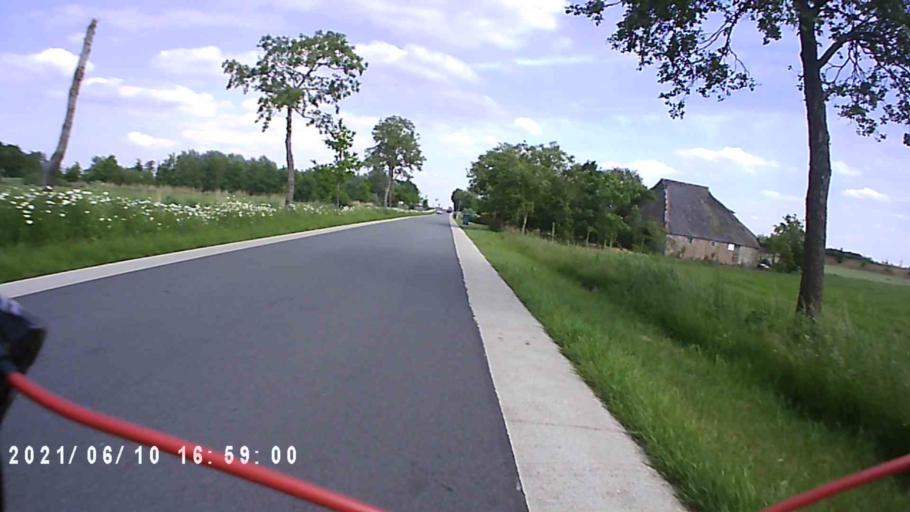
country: NL
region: Friesland
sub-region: Gemeente Kollumerland en Nieuwkruisland
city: Kollum
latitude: 53.2706
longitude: 6.1536
